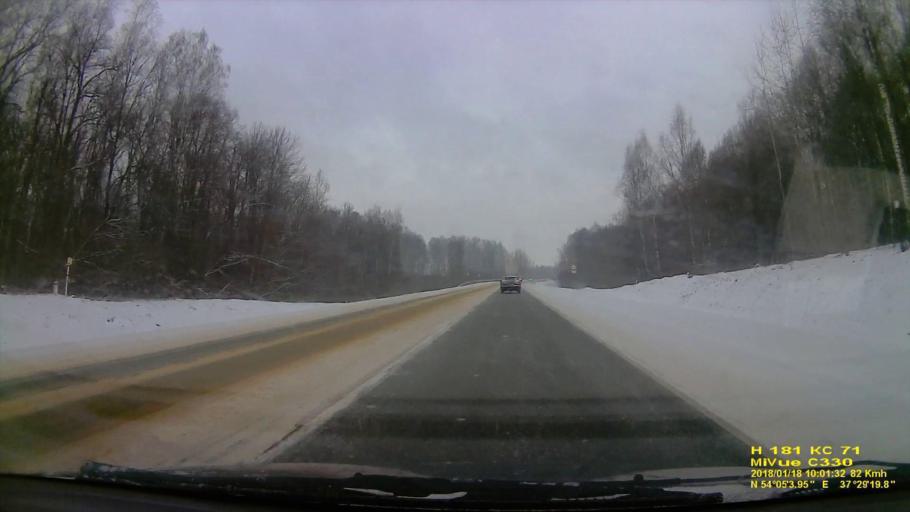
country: RU
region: Tula
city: Pervomayskiy
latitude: 54.0847
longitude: 37.4888
